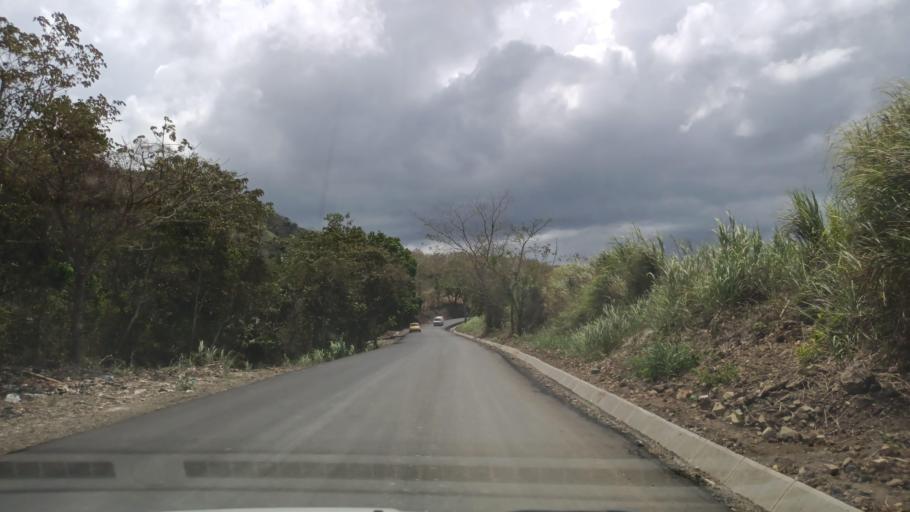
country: PA
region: Panama
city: Alcalde Diaz
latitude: 9.0913
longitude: -79.5774
